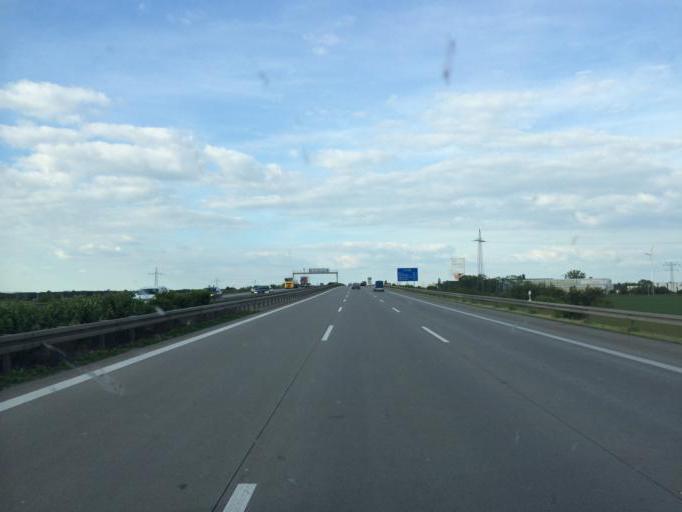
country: DE
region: Saxony-Anhalt
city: Barleben
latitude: 52.1967
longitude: 11.6396
